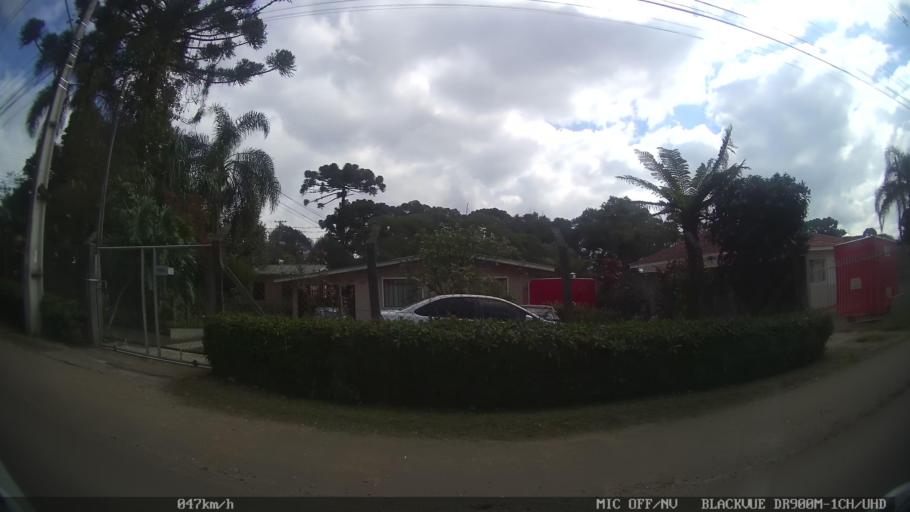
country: BR
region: Parana
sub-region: Pinhais
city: Pinhais
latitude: -25.3703
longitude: -49.2166
